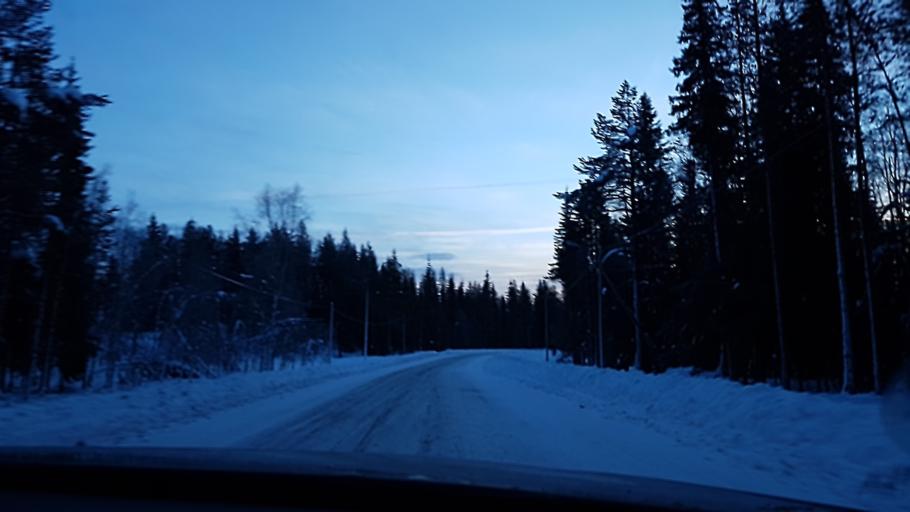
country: SE
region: Norrbotten
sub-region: Jokkmokks Kommun
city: Jokkmokk
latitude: 66.1419
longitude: 19.9983
